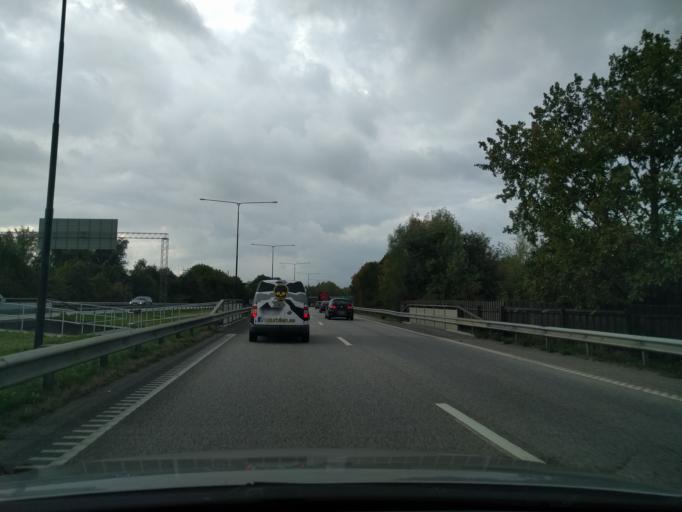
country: SE
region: Skane
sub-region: Malmo
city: Malmoe
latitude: 55.5650
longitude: 13.0368
